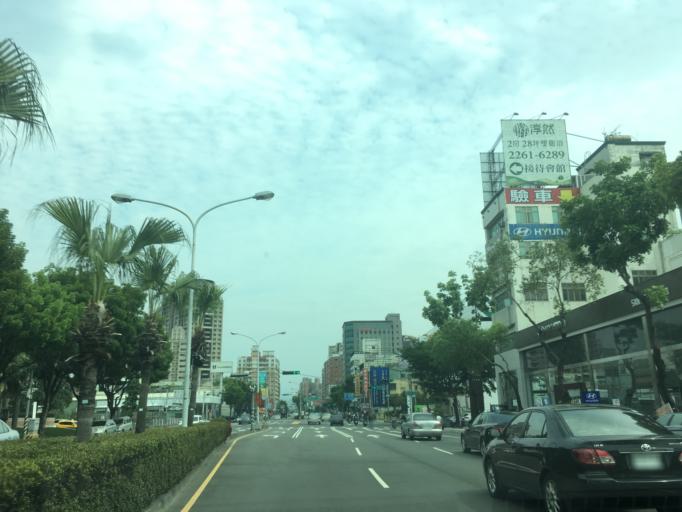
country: TW
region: Taiwan
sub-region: Taichung City
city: Taichung
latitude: 24.1174
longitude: 120.6532
